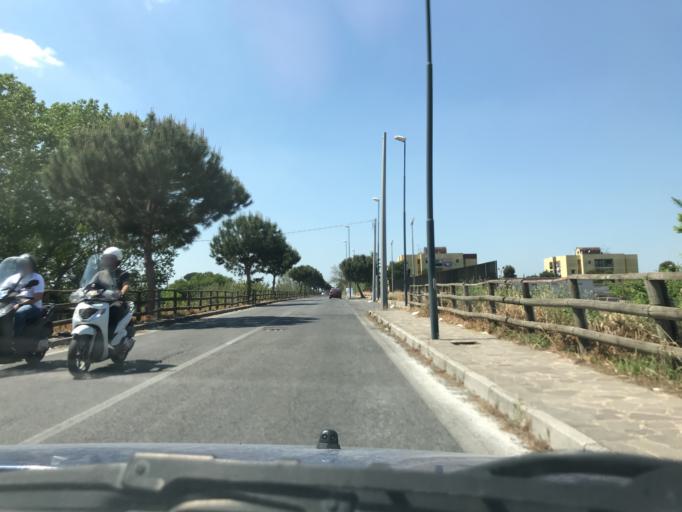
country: IT
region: Campania
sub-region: Provincia di Napoli
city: Villaricca
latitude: 40.9158
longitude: 14.1783
